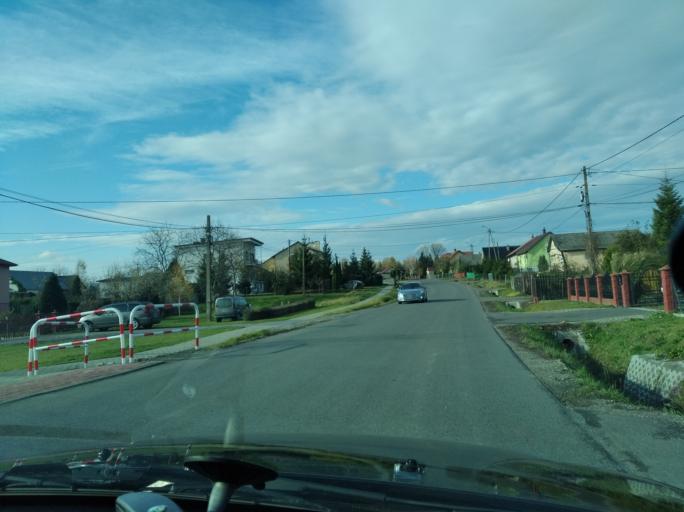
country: PL
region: Subcarpathian Voivodeship
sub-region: Powiat ropczycko-sedziszowski
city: Sedziszow Malopolski
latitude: 50.0802
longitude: 21.7305
